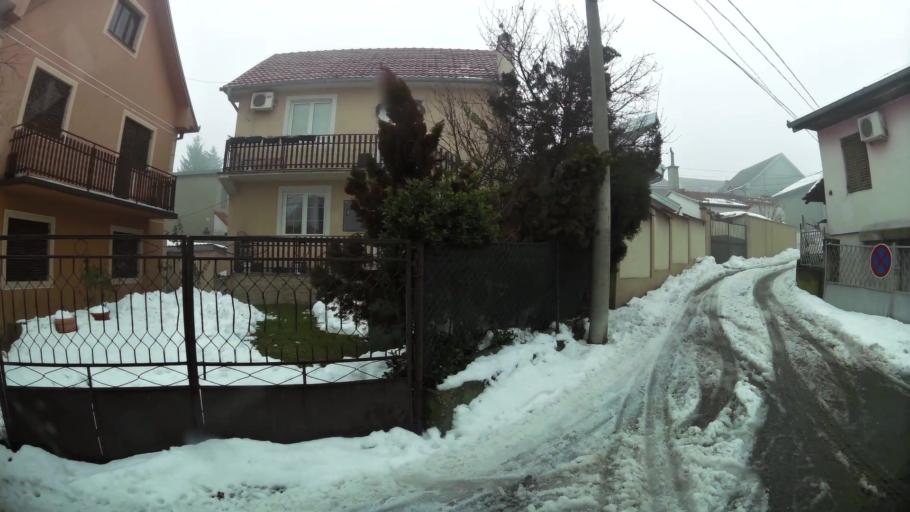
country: RS
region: Central Serbia
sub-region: Belgrade
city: Zvezdara
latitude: 44.7781
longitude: 20.5337
